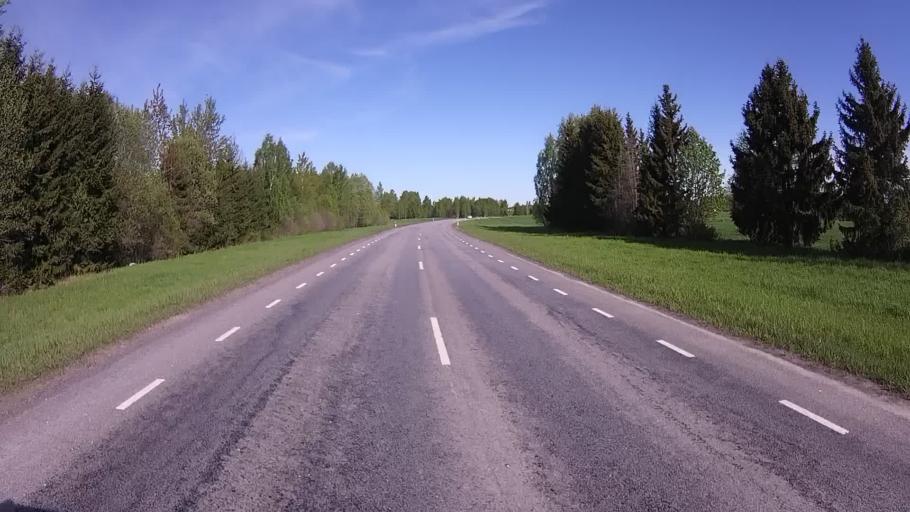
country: EE
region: Polvamaa
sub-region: Polva linn
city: Polva
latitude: 58.2446
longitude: 27.0063
